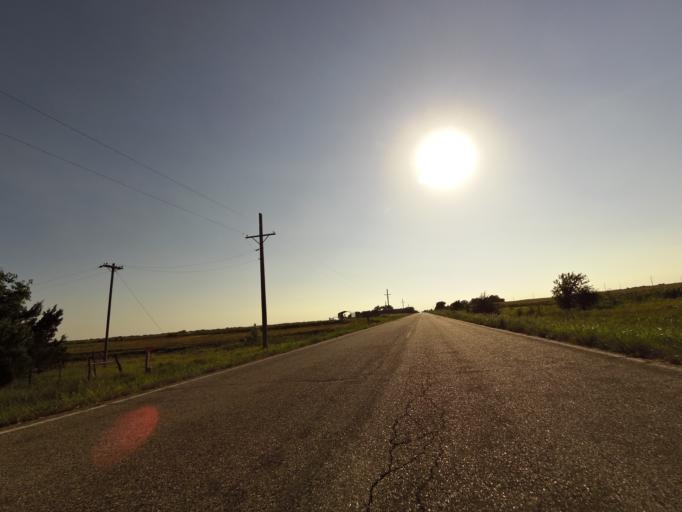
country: US
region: Kansas
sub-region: McPherson County
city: Moundridge
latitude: 38.1451
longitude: -97.5864
